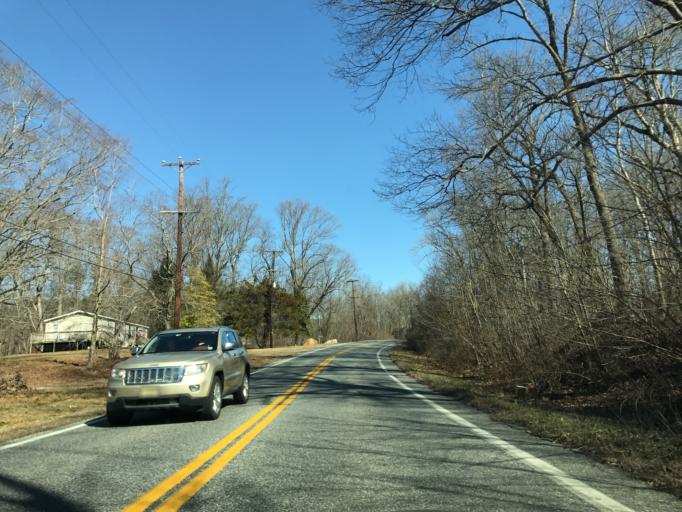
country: US
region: Maryland
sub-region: Cecil County
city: Charlestown
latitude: 39.5926
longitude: -75.9708
